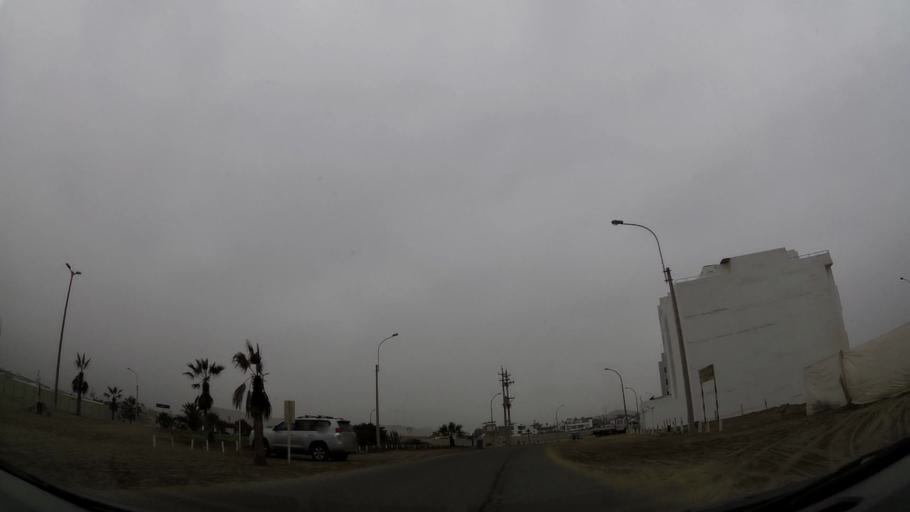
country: PE
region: Lima
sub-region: Lima
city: Punta Hermosa
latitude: -12.3282
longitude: -76.8319
